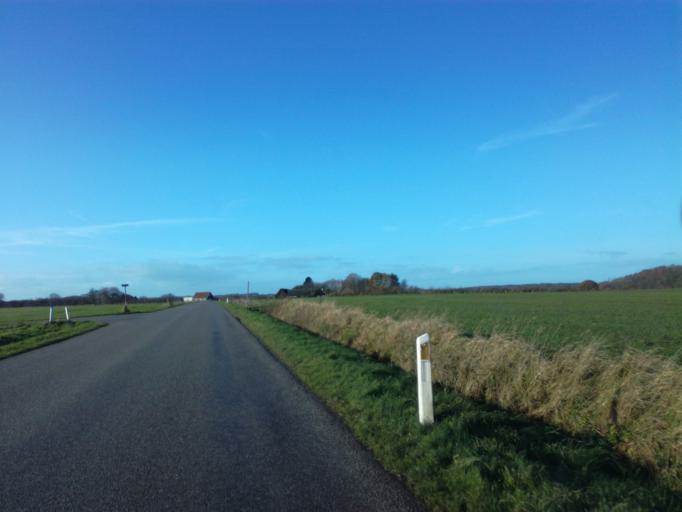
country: DK
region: South Denmark
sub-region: Fredericia Kommune
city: Taulov
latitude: 55.5711
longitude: 9.6532
